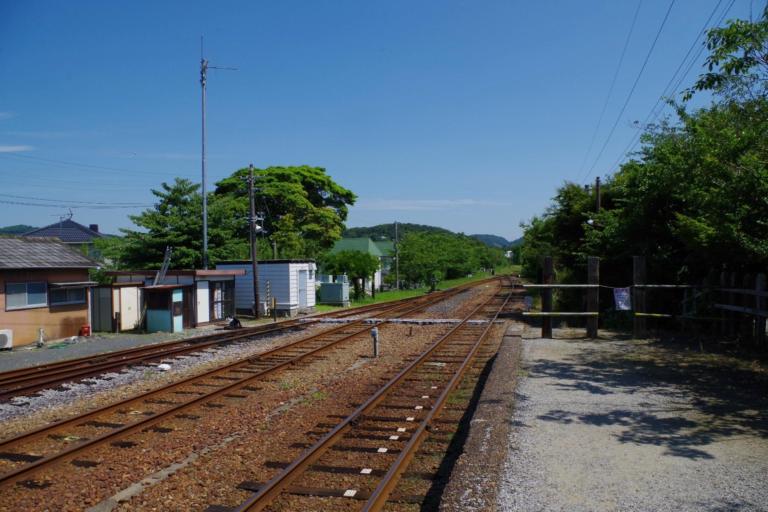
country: JP
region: Chiba
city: Mobara
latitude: 35.2870
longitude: 140.2440
